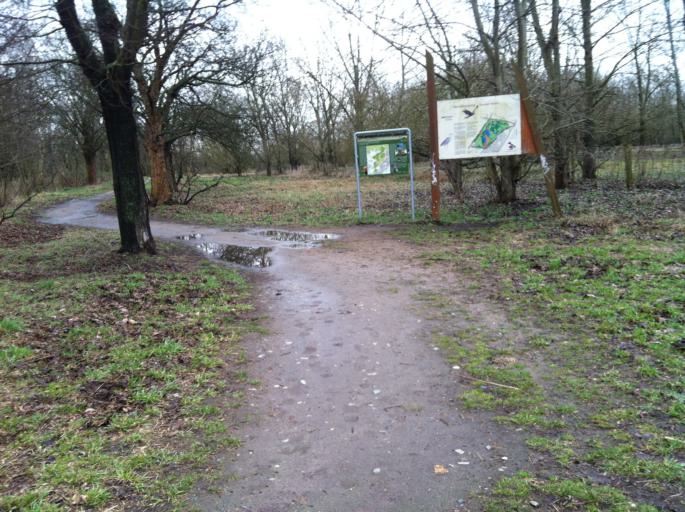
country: DE
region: Berlin
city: Karow
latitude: 52.6233
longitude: 13.4567
